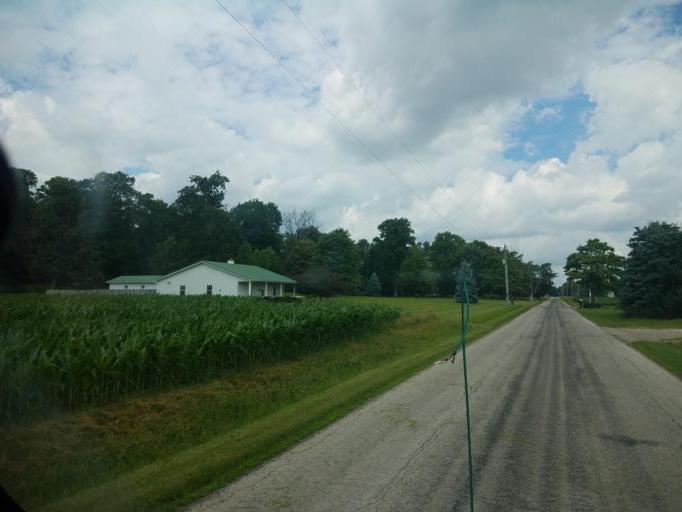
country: US
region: Ohio
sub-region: Richland County
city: Shelby
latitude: 40.9353
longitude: -82.7050
